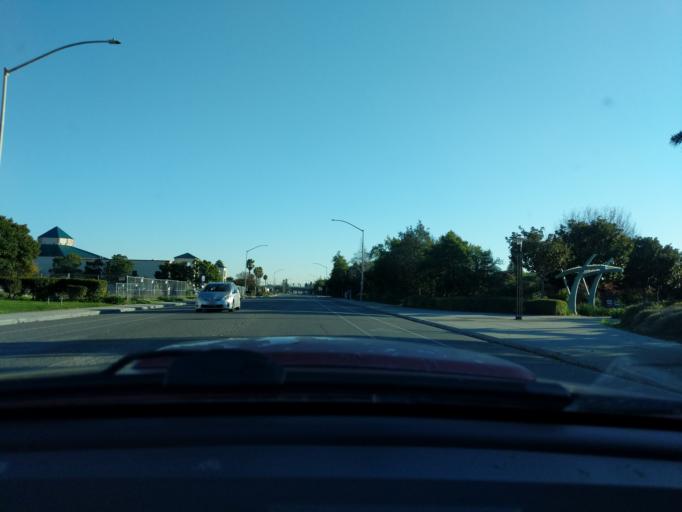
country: US
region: California
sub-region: Santa Clara County
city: Milpitas
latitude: 37.4207
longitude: -121.9173
